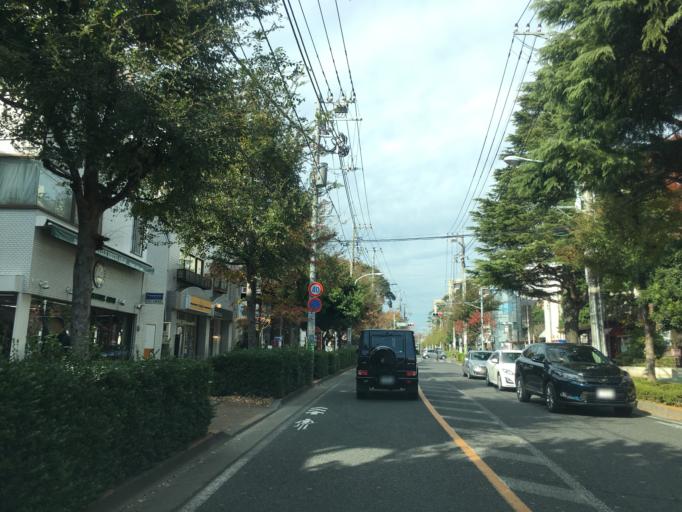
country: JP
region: Tokyo
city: Chofugaoka
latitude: 35.6343
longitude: 139.5780
